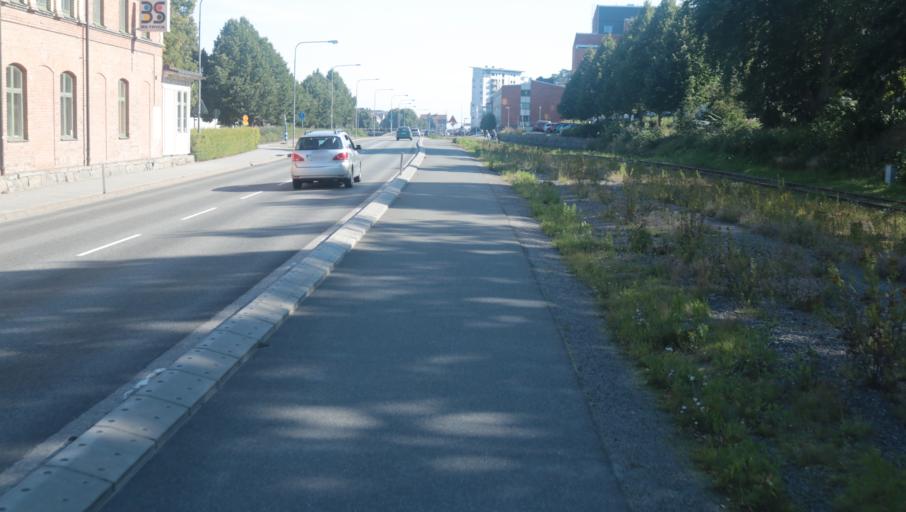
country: SE
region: Blekinge
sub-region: Karlshamns Kommun
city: Karlshamn
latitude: 56.1732
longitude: 14.8567
